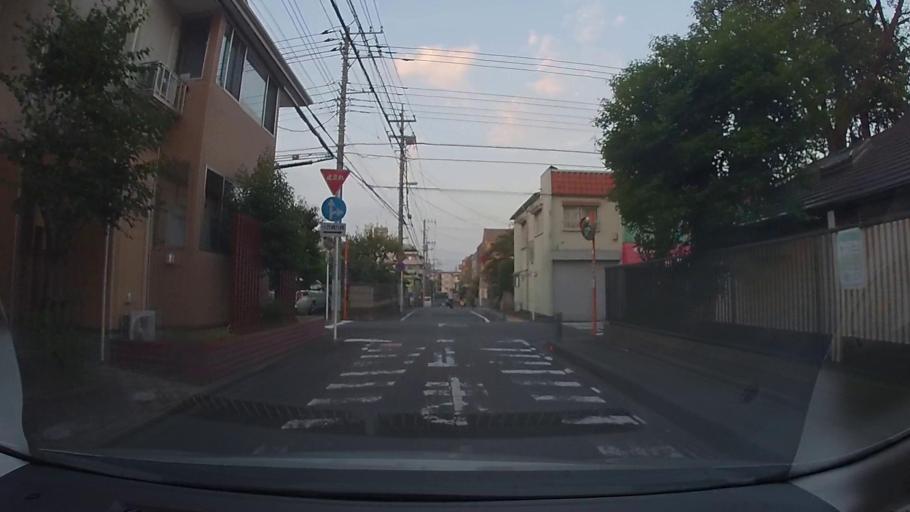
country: JP
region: Kanagawa
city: Minami-rinkan
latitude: 35.4970
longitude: 139.4447
